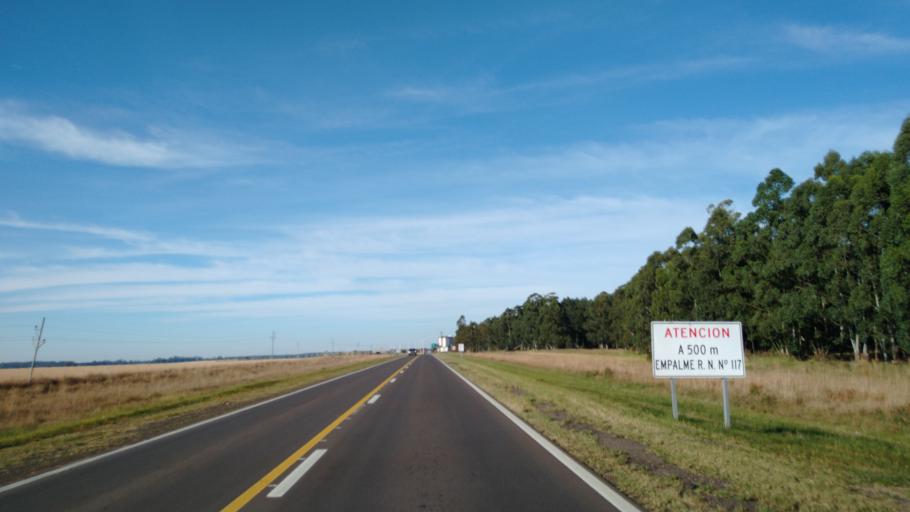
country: AR
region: Corrientes
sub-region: Departamento de Paso de los Libres
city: Paso de los Libres
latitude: -29.7013
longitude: -57.2114
